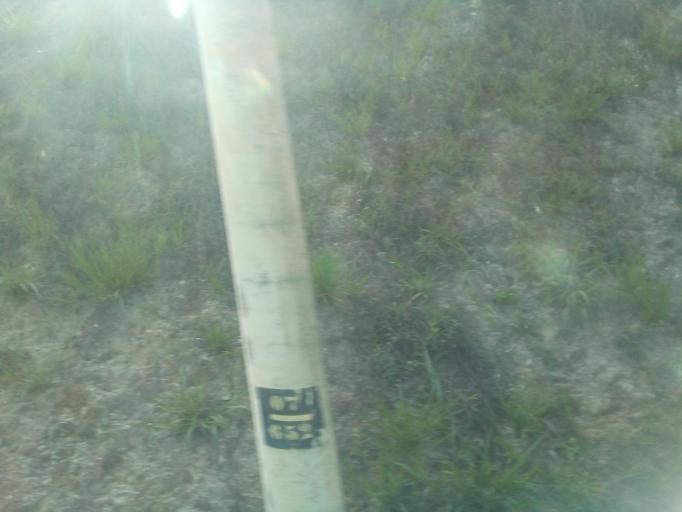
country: BR
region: Minas Gerais
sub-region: Belo Horizonte
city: Belo Horizonte
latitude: -19.8851
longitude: -43.8643
